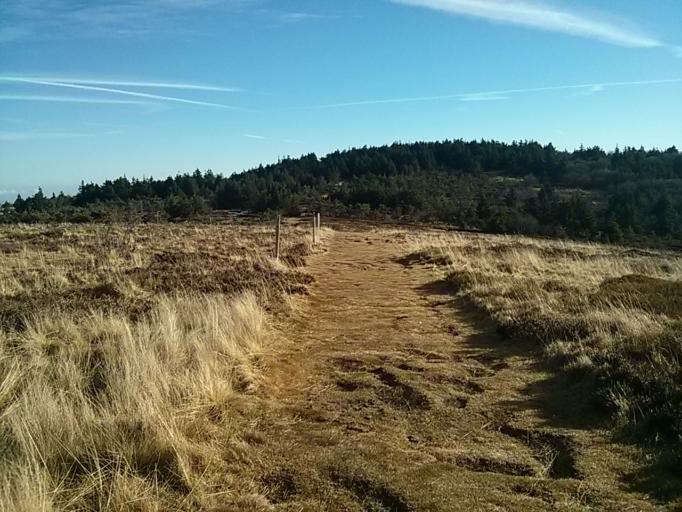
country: FR
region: Rhone-Alpes
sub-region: Departement de la Loire
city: Saint-Julien-Molin-Molette
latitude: 45.3826
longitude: 4.5743
